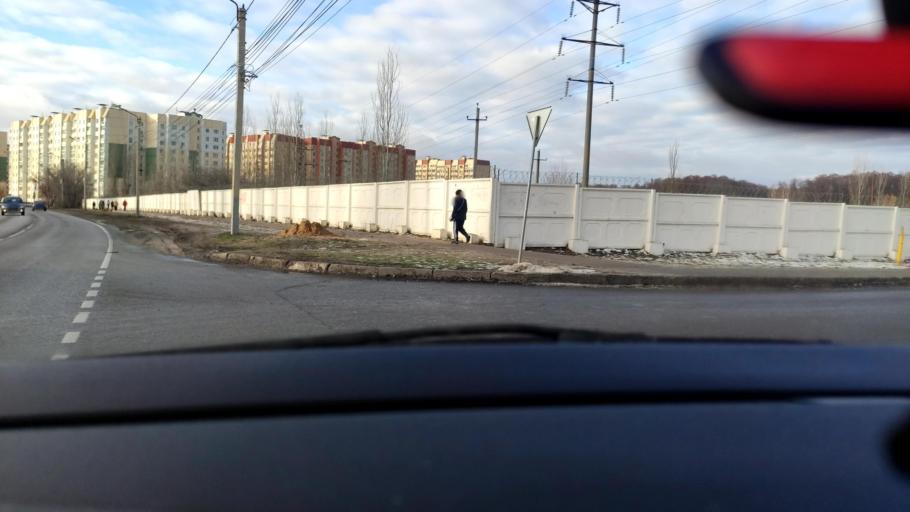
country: RU
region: Voronezj
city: Pridonskoy
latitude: 51.6222
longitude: 39.0696
